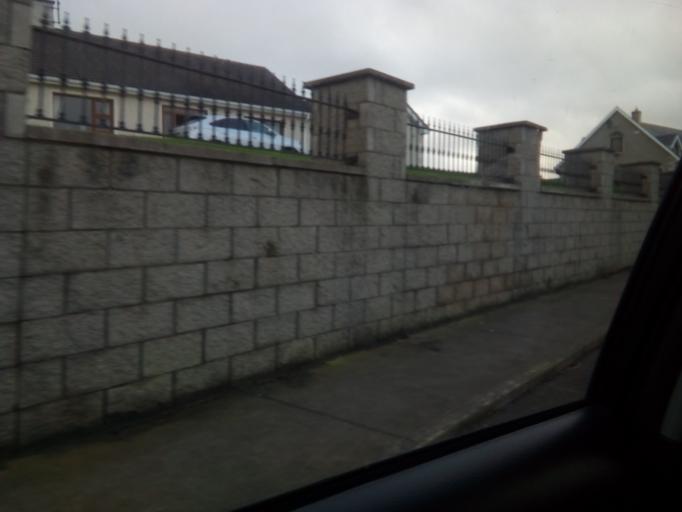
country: IE
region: Leinster
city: An Ros
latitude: 53.5223
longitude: -6.0796
